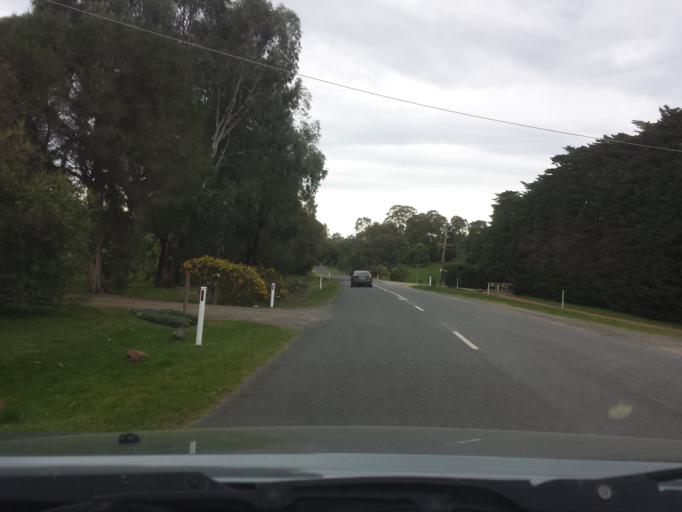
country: AU
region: Victoria
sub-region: Yarra Ranges
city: Yarra Glen
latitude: -37.6398
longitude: 145.3745
